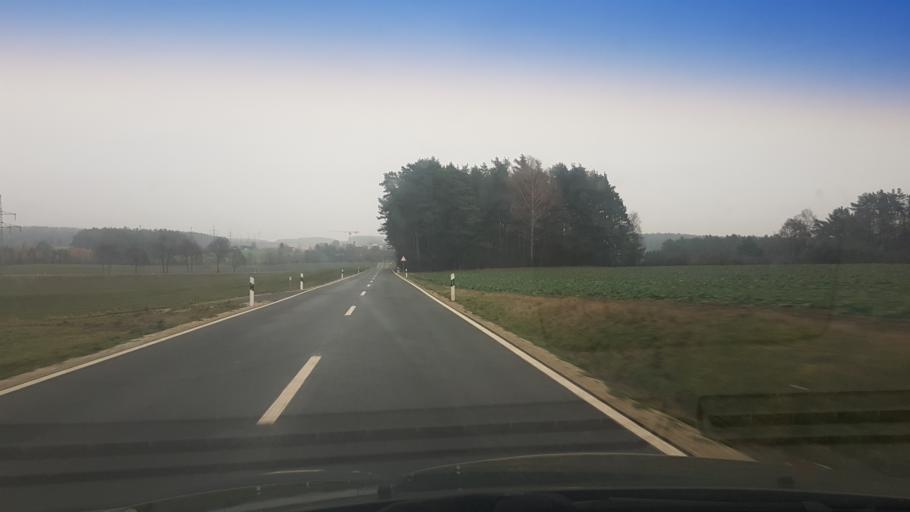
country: DE
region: Bavaria
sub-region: Upper Franconia
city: Wonsees
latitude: 50.0277
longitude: 11.2900
